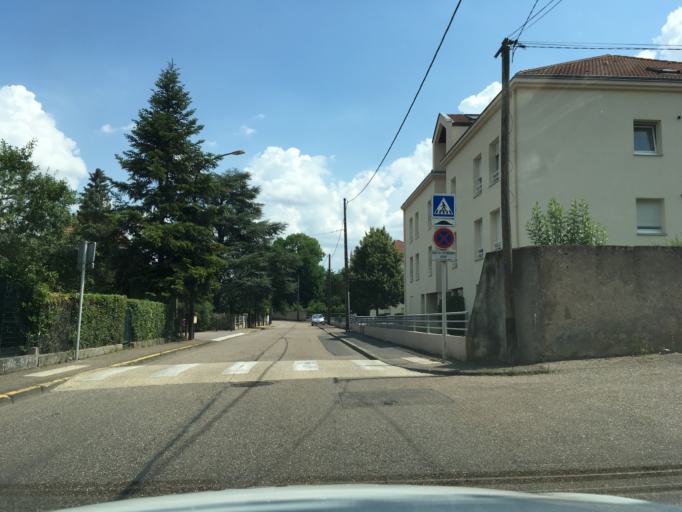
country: FR
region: Lorraine
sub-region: Departement de la Moselle
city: Saint-Julien-les-Metz
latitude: 49.1212
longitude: 6.2010
